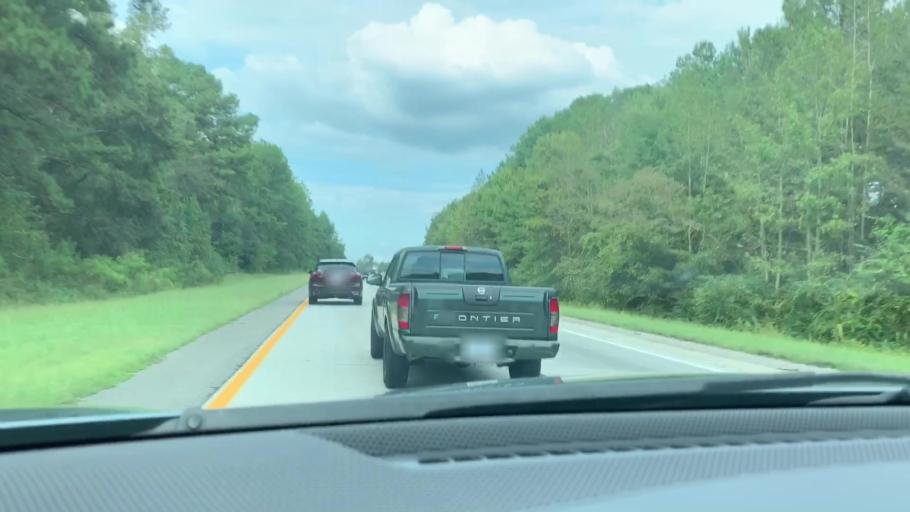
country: US
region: South Carolina
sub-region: Dorchester County
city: Saint George
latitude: 33.1225
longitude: -80.6405
